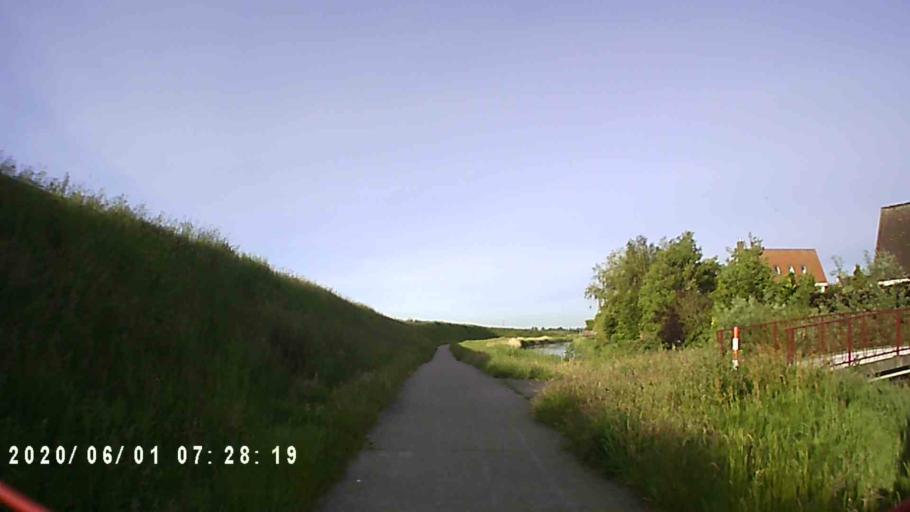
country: NL
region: Friesland
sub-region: Gemeente Dongeradeel
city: Dokkum
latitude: 53.3147
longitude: 6.0152
